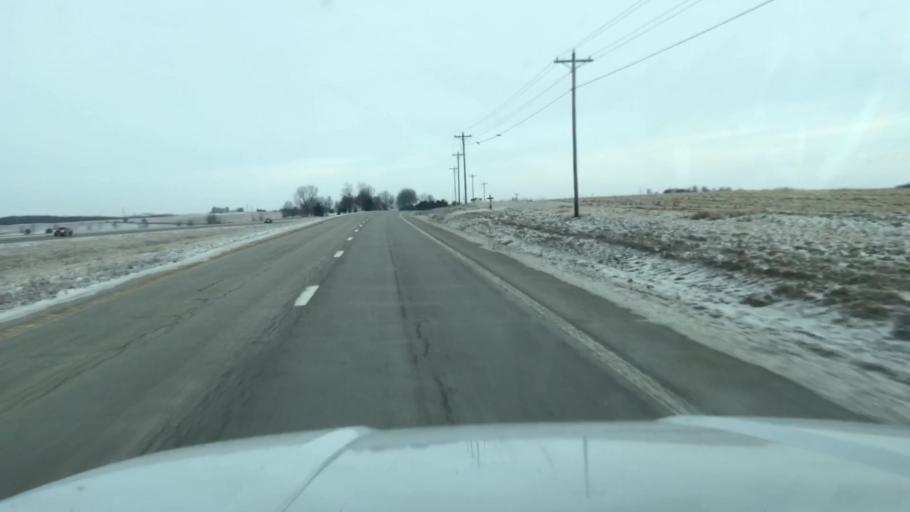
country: US
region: Missouri
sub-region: Andrew County
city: Savannah
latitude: 39.9821
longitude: -94.8790
